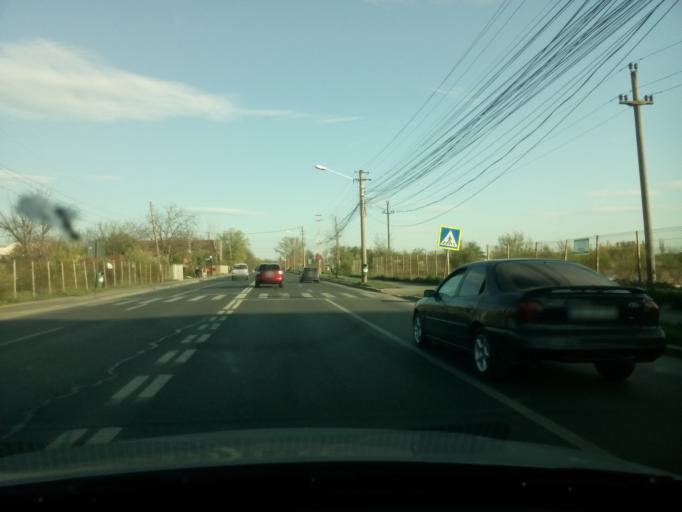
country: RO
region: Ilfov
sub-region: Comuna Mogosoaia
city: Mogosoaia
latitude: 44.5094
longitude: 26.0225
